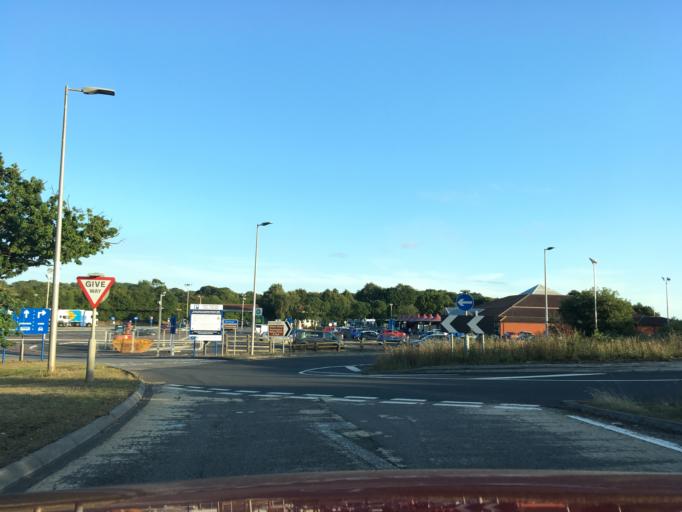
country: GB
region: England
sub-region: West Berkshire
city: Winterbourne
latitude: 51.4503
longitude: -1.3106
